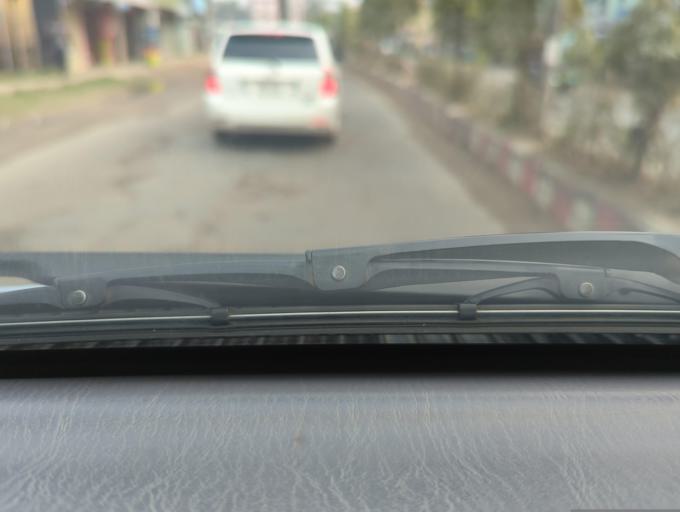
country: BD
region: Sylhet
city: Maulavi Bazar
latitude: 24.4887
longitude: 91.7495
